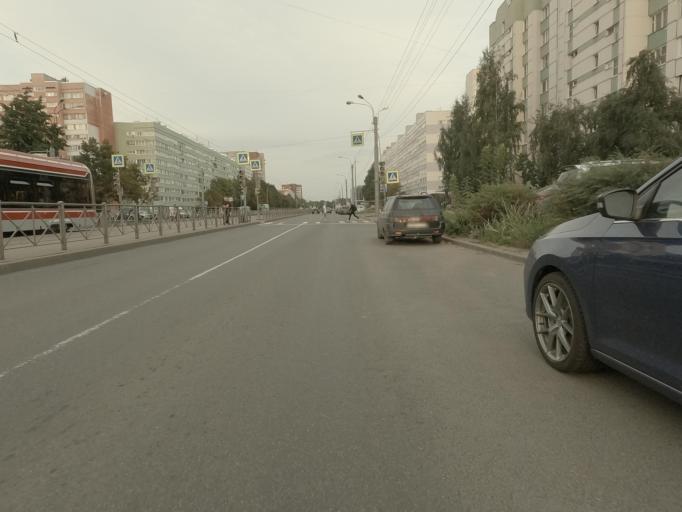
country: RU
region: St.-Petersburg
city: Dachnoye
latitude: 59.8595
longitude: 30.2392
